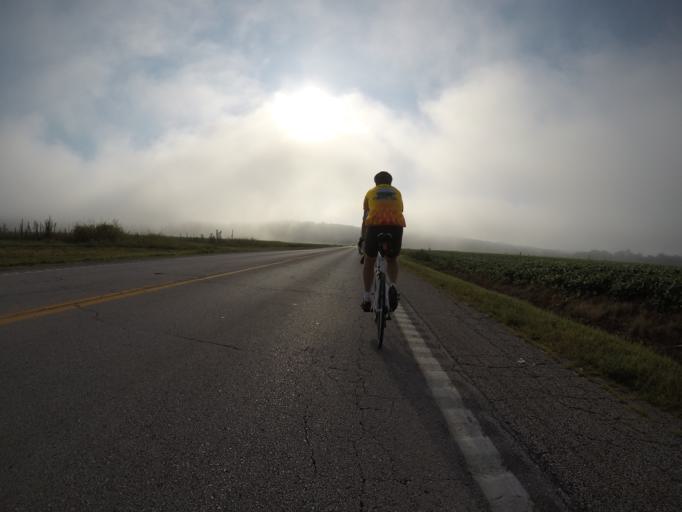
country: US
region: Kansas
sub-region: Leavenworth County
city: Leavenworth
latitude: 39.3245
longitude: -94.8644
